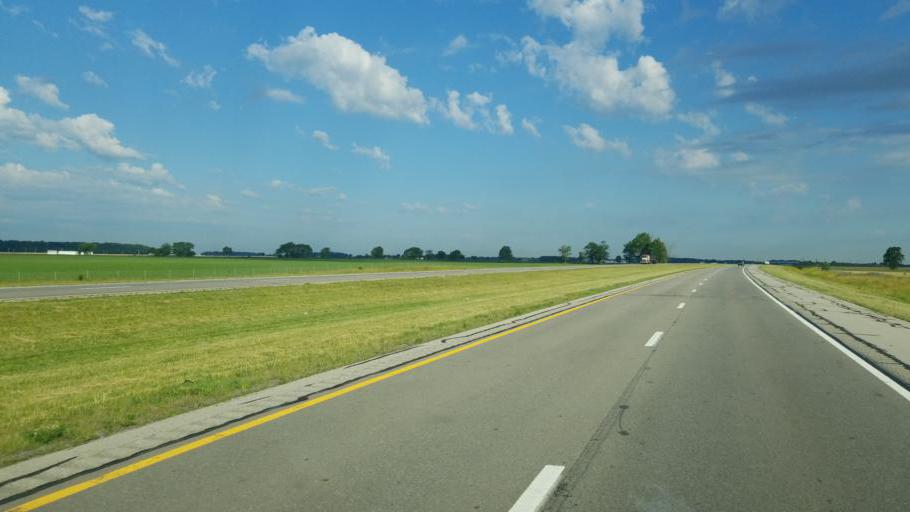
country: US
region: Ohio
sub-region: Crawford County
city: Bucyrus
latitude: 40.7744
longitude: -82.8864
